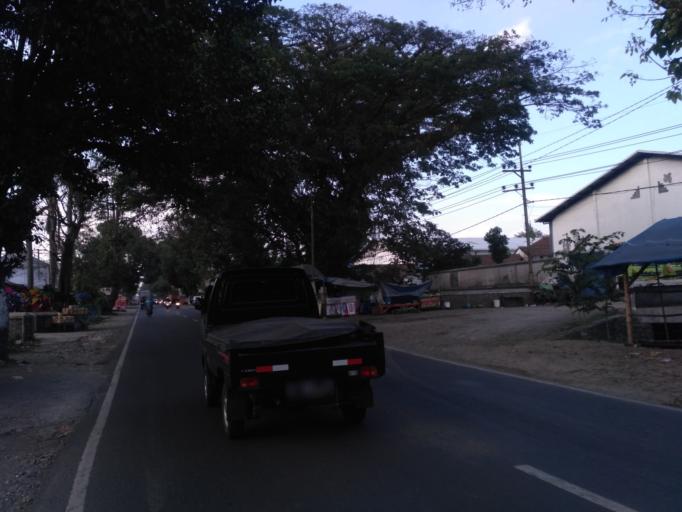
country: ID
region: East Java
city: Kebonsari
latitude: -8.0324
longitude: 112.6138
